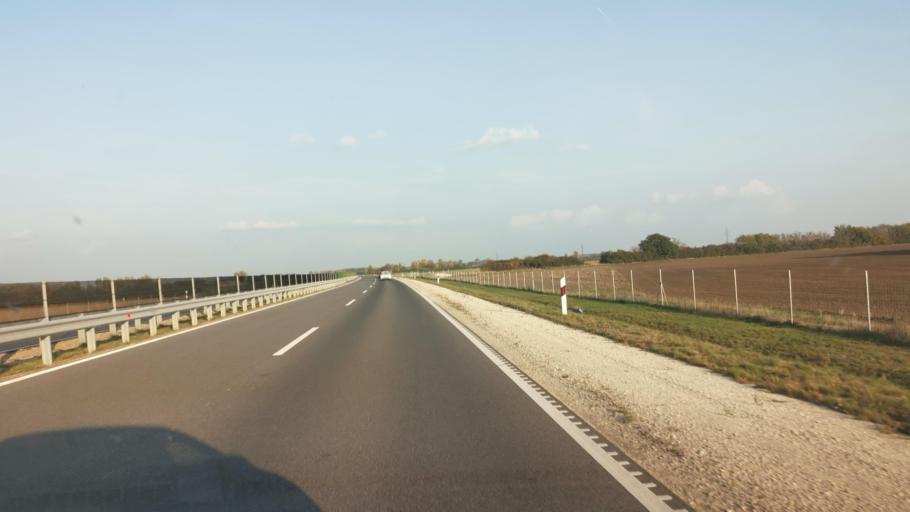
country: HU
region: Gyor-Moson-Sopron
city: Mihalyi
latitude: 47.5648
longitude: 17.1206
